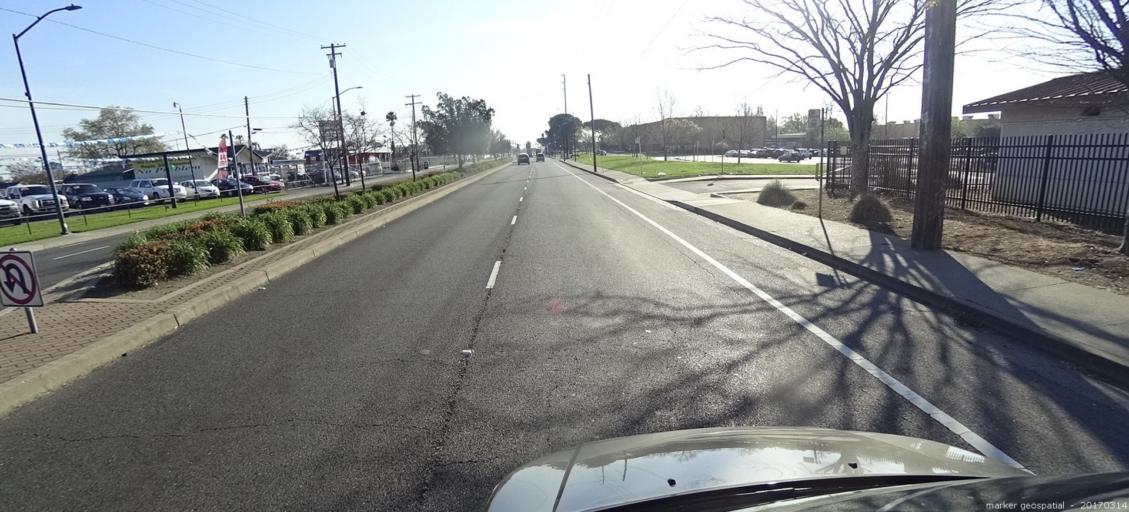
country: US
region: California
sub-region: Sacramento County
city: Parkway
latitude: 38.4959
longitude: -121.4694
